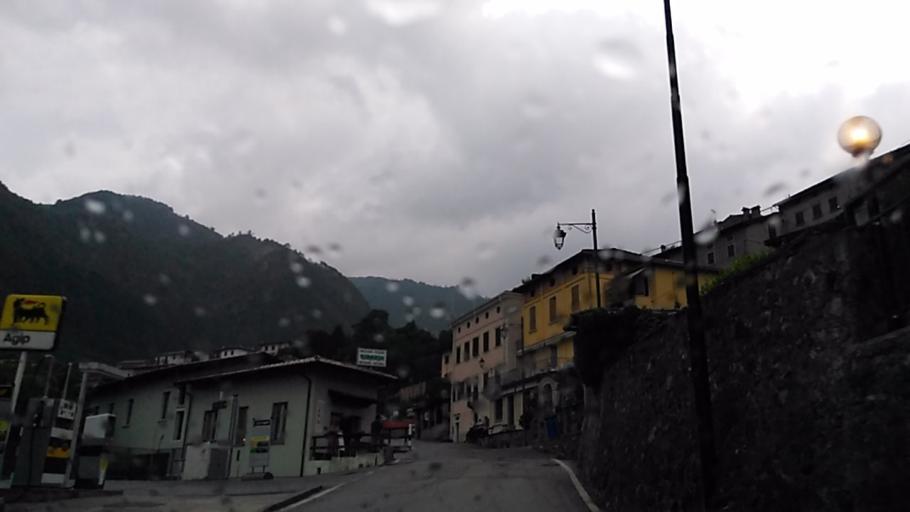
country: IT
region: Lombardy
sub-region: Provincia di Brescia
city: Pieve
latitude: 45.7920
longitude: 10.7447
